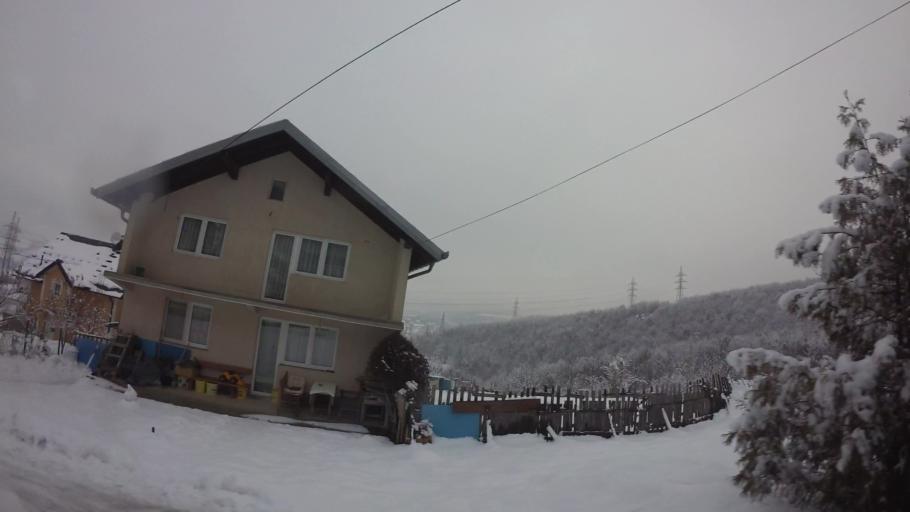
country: BA
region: Federation of Bosnia and Herzegovina
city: Vogosca
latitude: 43.8792
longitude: 18.3209
